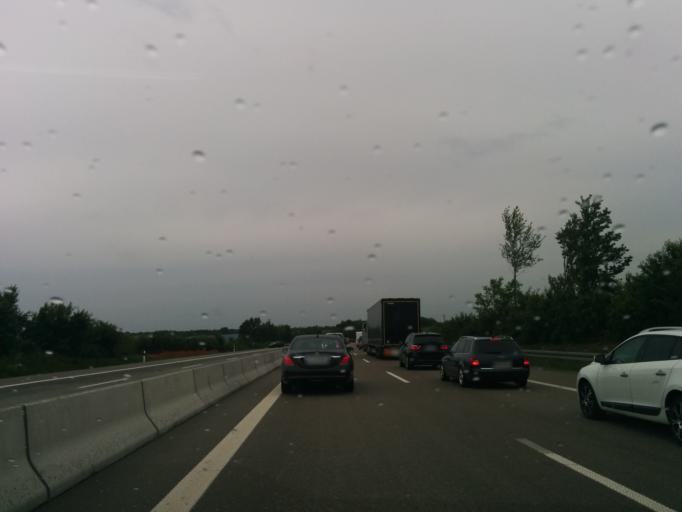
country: DE
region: Bavaria
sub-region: Regierungsbezirk Unterfranken
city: Martinsheim
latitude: 49.6140
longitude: 10.1721
